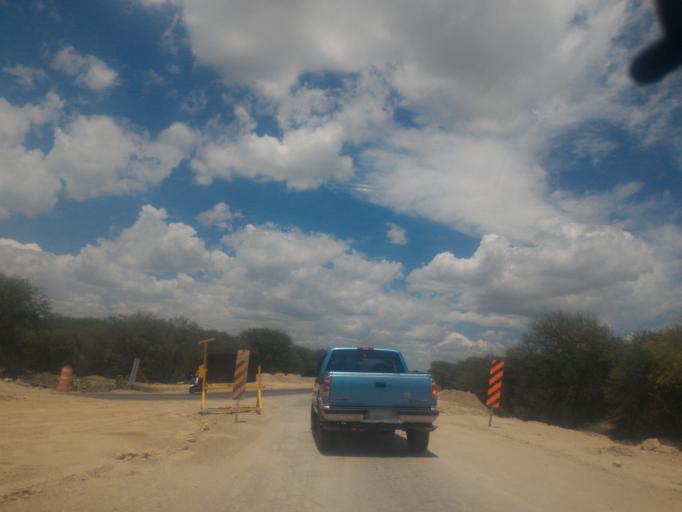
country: MX
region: Guanajuato
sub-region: Purisima del Rincon
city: Monte Grande
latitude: 21.0150
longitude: -101.8889
